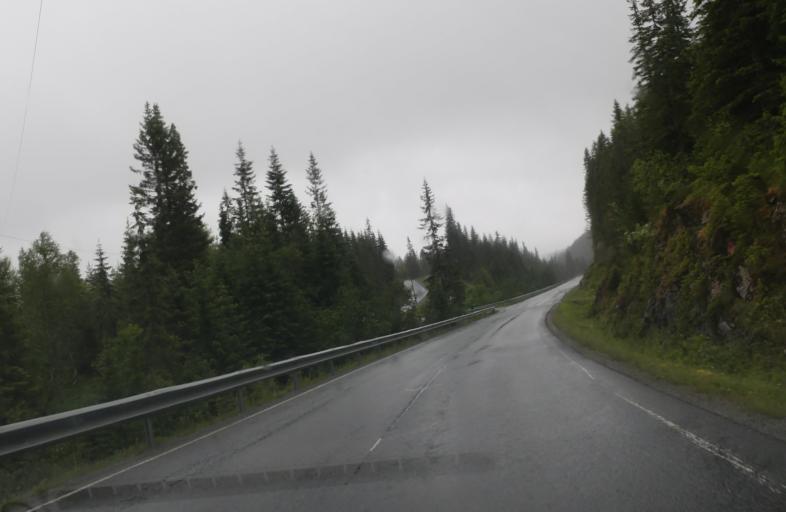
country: NO
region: Sor-Trondelag
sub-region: Selbu
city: Mebonden
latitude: 63.3352
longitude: 11.0934
